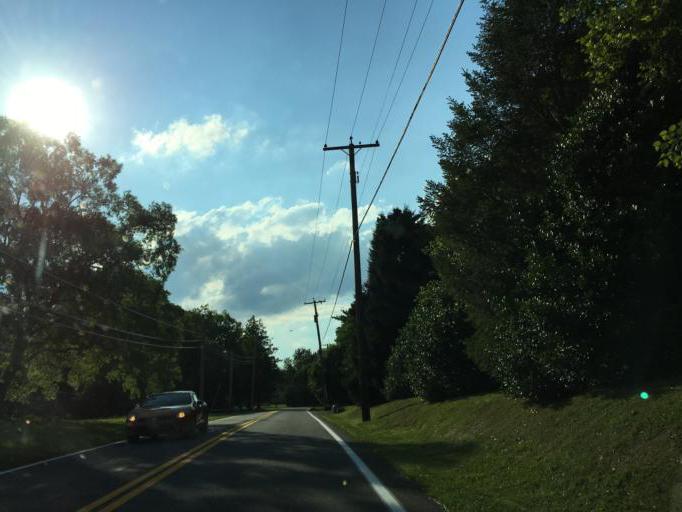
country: US
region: Maryland
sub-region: Baltimore County
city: Kingsville
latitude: 39.4695
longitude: -76.4440
